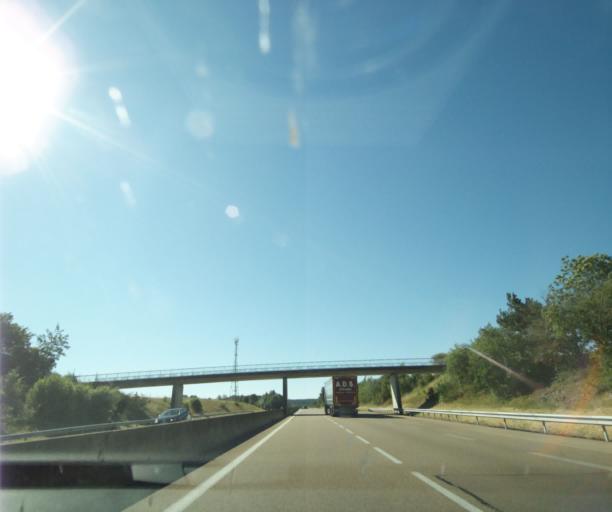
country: FR
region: Champagne-Ardenne
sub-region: Departement de la Haute-Marne
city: Chamarandes-Choignes
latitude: 47.9664
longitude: 5.1455
